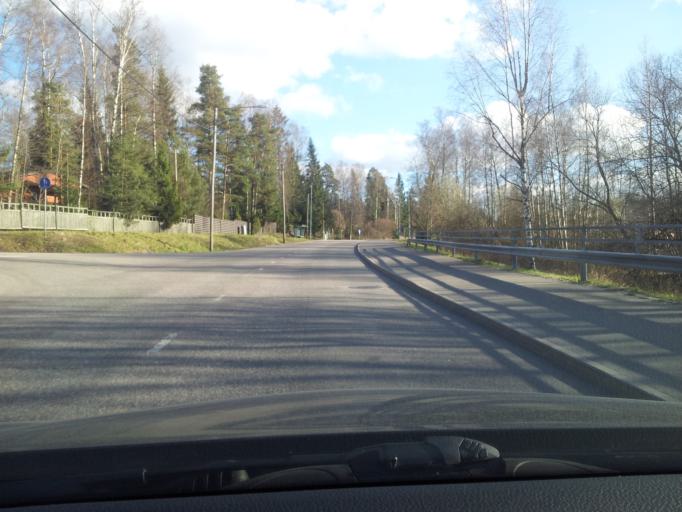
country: FI
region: Uusimaa
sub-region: Helsinki
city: Espoo
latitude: 60.1343
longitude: 24.6812
